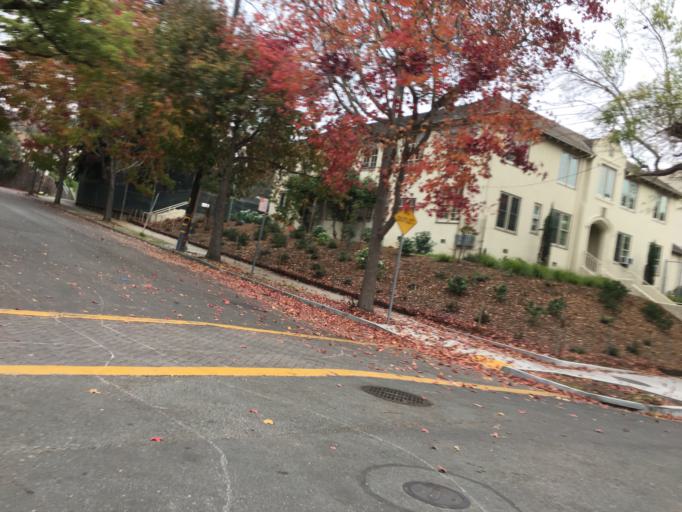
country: US
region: California
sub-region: Alameda County
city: Berkeley
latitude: 37.8855
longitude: -122.2723
